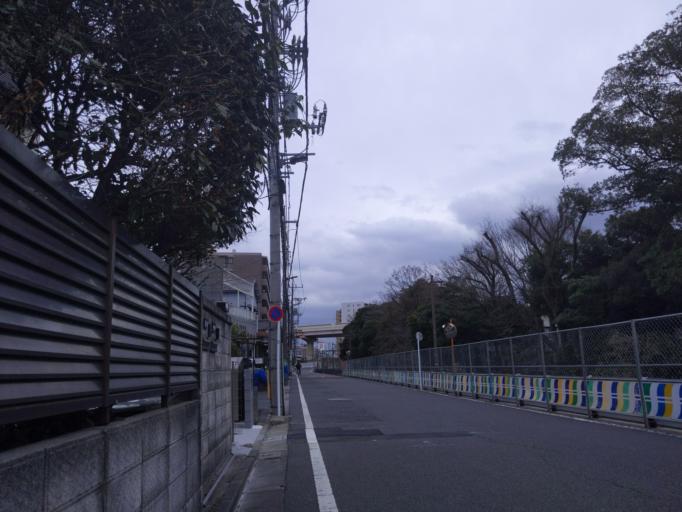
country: JP
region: Saitama
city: Soka
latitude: 35.7606
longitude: 139.8170
